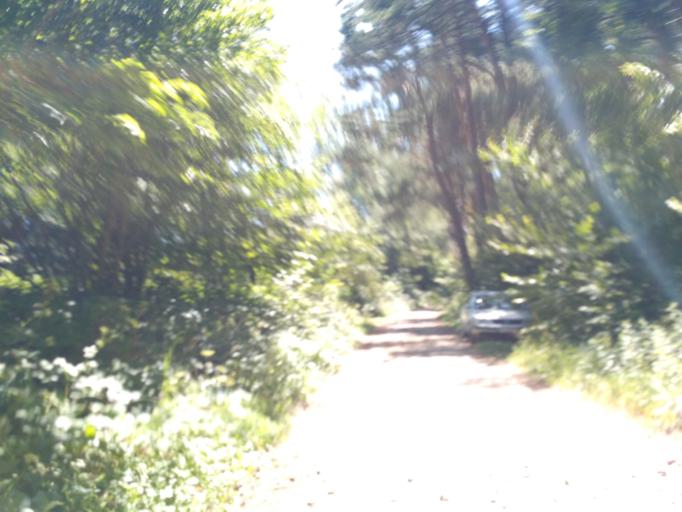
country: PL
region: Subcarpathian Voivodeship
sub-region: Powiat sanocki
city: Bukowsko
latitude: 49.4855
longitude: 22.0935
